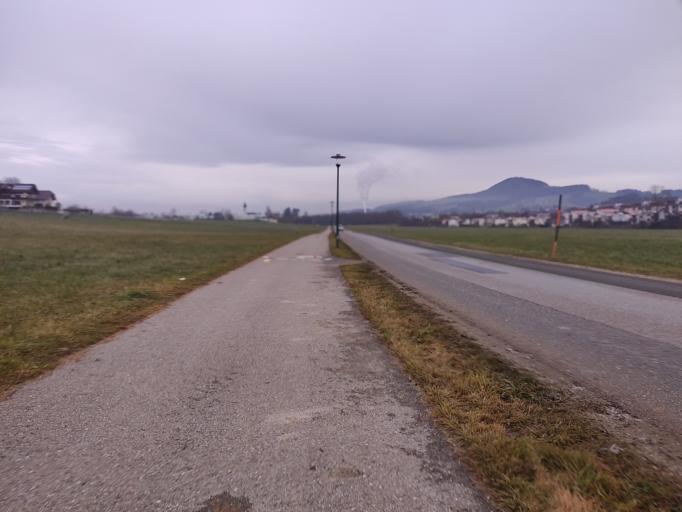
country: AT
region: Salzburg
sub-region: Politischer Bezirk Salzburg-Umgebung
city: Obertrum am See
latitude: 47.9278
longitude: 13.0742
